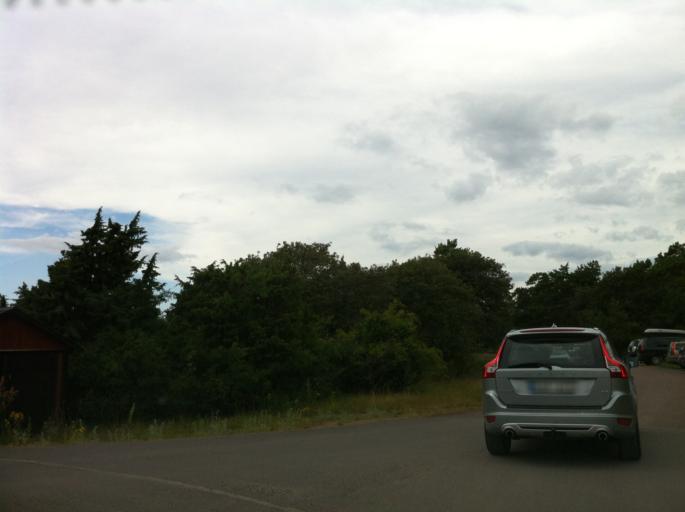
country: SE
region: Kalmar
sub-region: Vasterviks Kommun
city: Vaestervik
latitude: 57.3668
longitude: 17.0913
